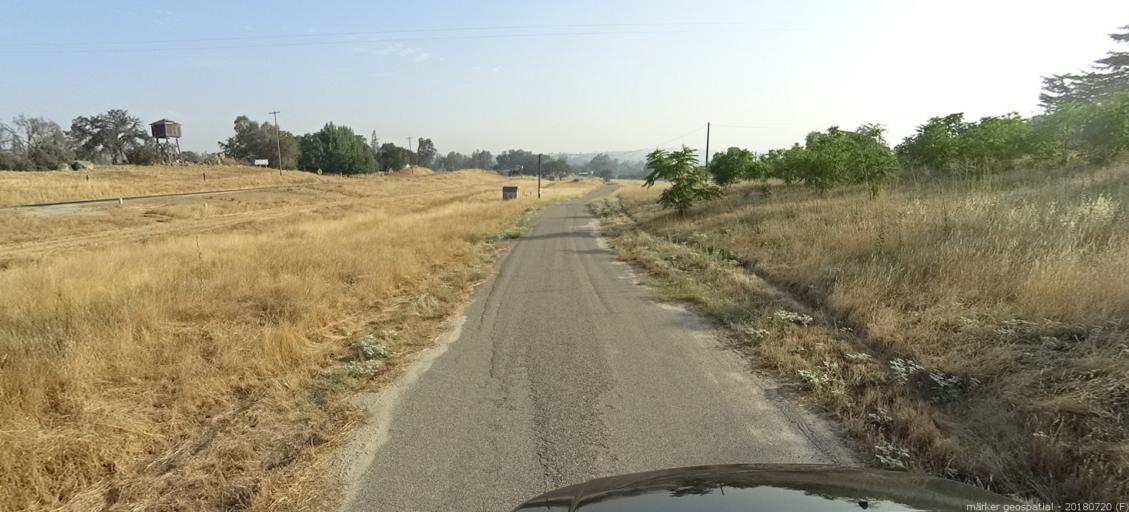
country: US
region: California
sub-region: Madera County
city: Yosemite Lakes
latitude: 37.2079
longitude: -119.9074
